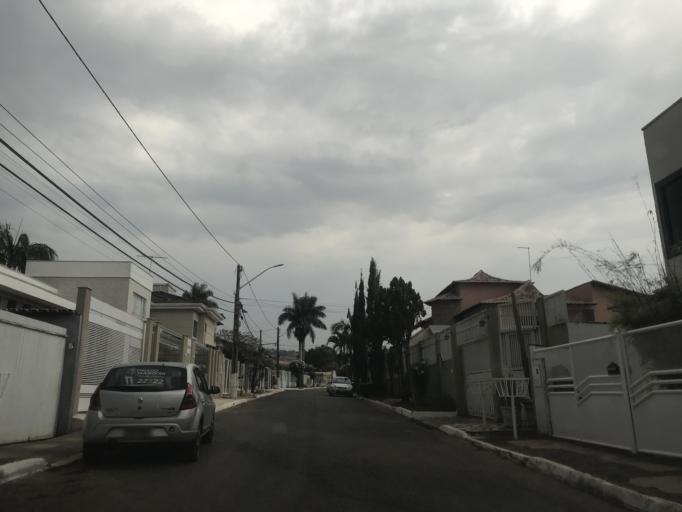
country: BR
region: Federal District
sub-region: Brasilia
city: Brasilia
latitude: -15.6630
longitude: -47.8325
